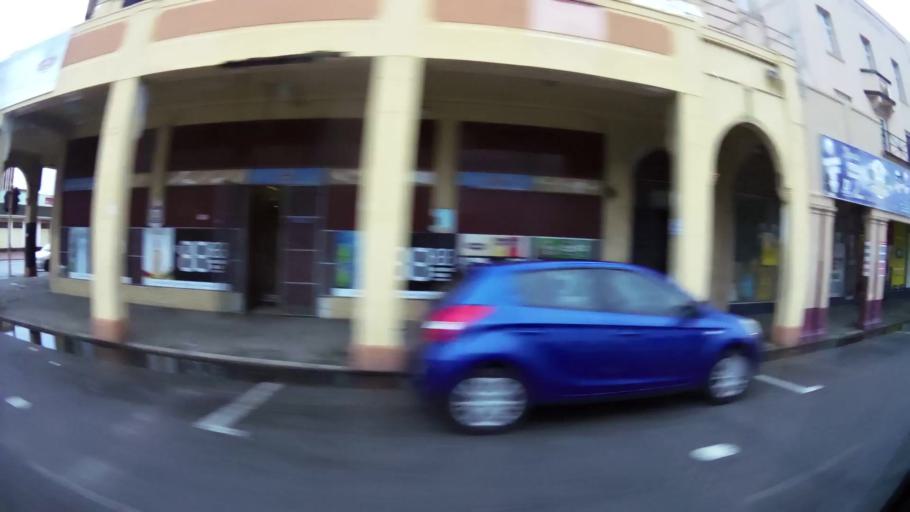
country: ZA
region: Eastern Cape
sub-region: Nelson Mandela Bay Metropolitan Municipality
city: Port Elizabeth
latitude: -33.9434
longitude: 25.6060
